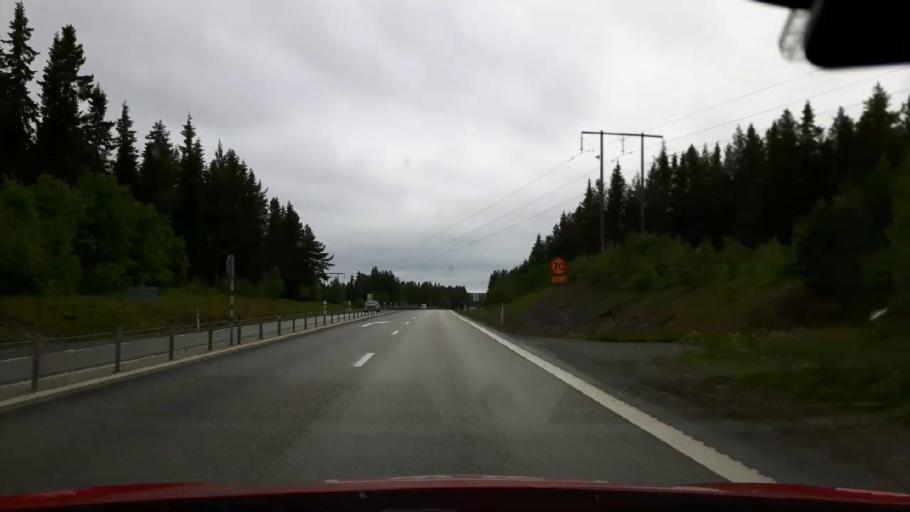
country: SE
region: Jaemtland
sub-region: OEstersunds Kommun
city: Brunflo
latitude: 63.1238
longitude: 14.7944
